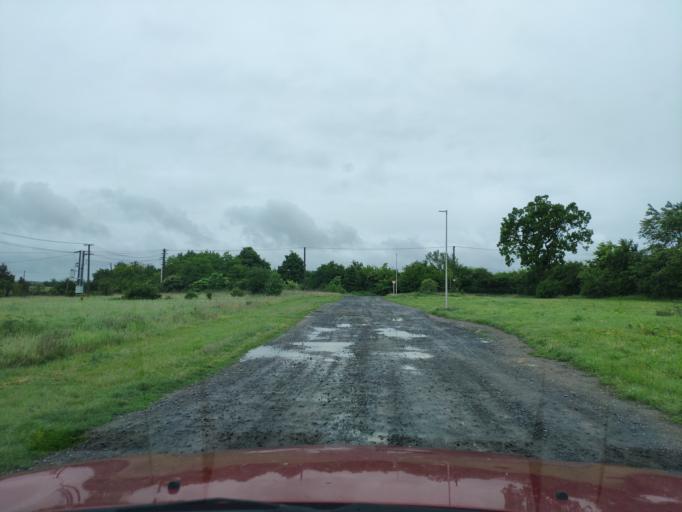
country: SK
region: Kosicky
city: Cierna nad Tisou
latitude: 48.4036
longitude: 22.0618
